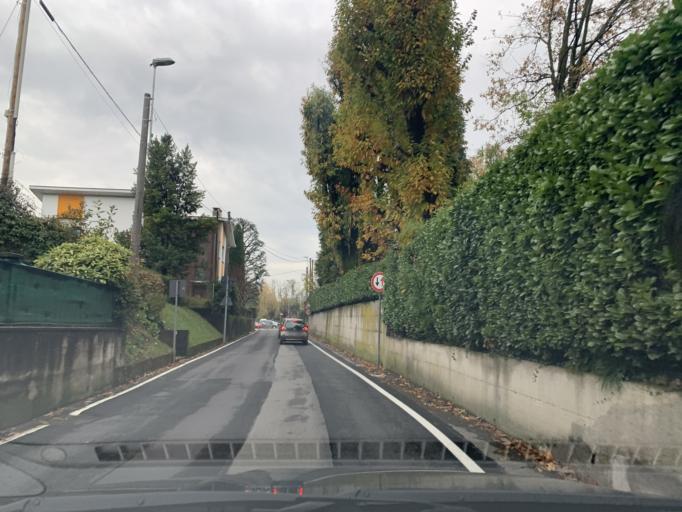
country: IT
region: Lombardy
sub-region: Provincia di Como
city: Bulgorello
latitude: 45.7235
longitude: 9.0539
